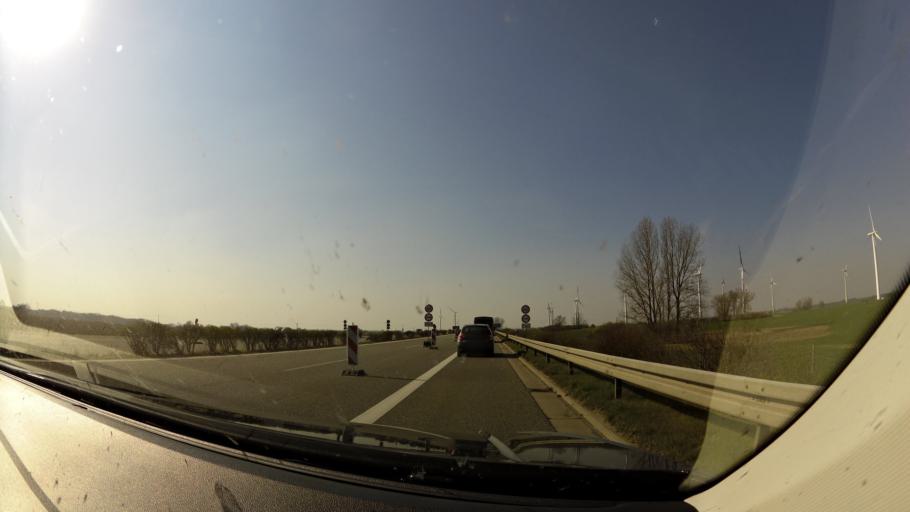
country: DE
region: Mecklenburg-Vorpommern
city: Grimmen
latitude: 54.0838
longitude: 13.0005
